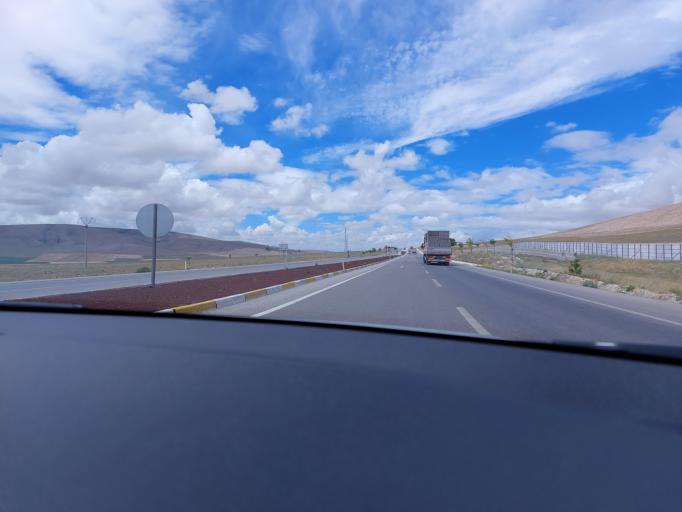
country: TR
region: Konya
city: Obruk
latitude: 38.0615
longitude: 33.0466
